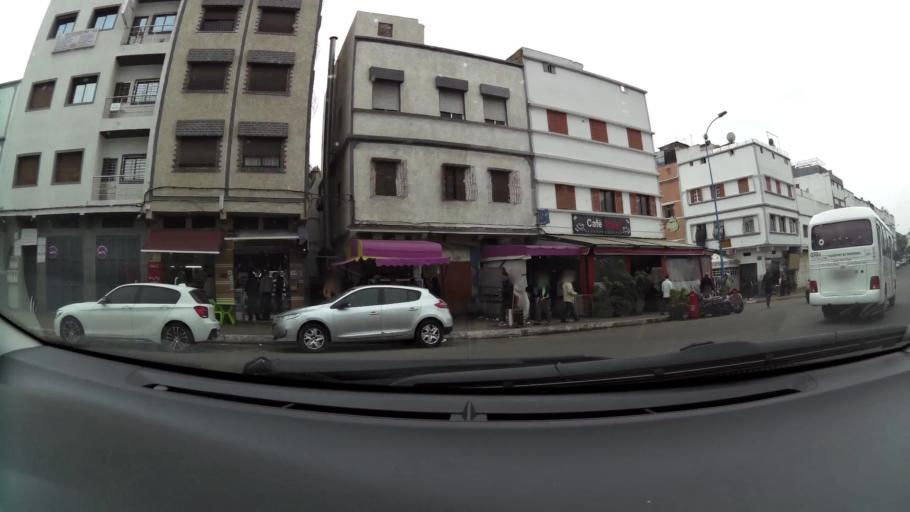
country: MA
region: Grand Casablanca
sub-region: Casablanca
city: Casablanca
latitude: 33.5623
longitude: -7.5627
